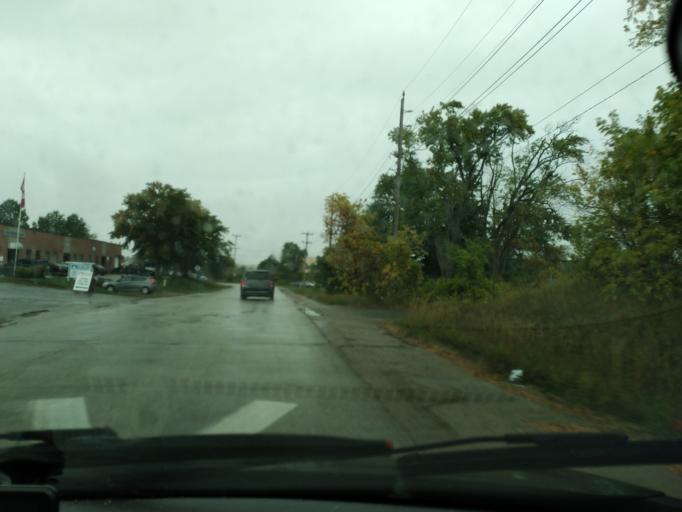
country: CA
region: Ontario
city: Barrie
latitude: 44.3556
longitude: -79.6675
